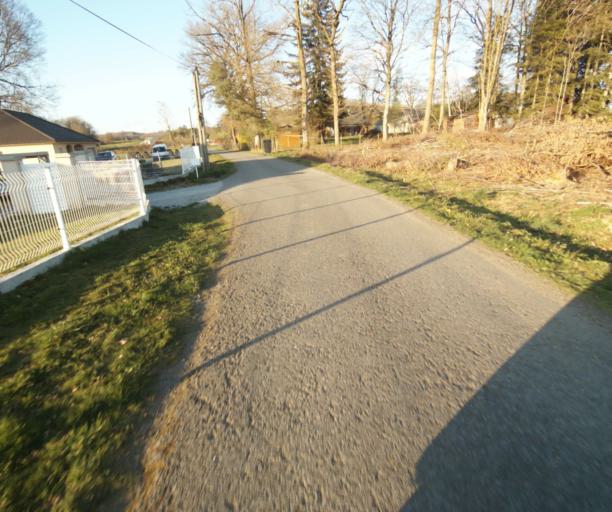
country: FR
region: Limousin
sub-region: Departement de la Correze
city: Uzerche
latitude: 45.3598
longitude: 1.5962
